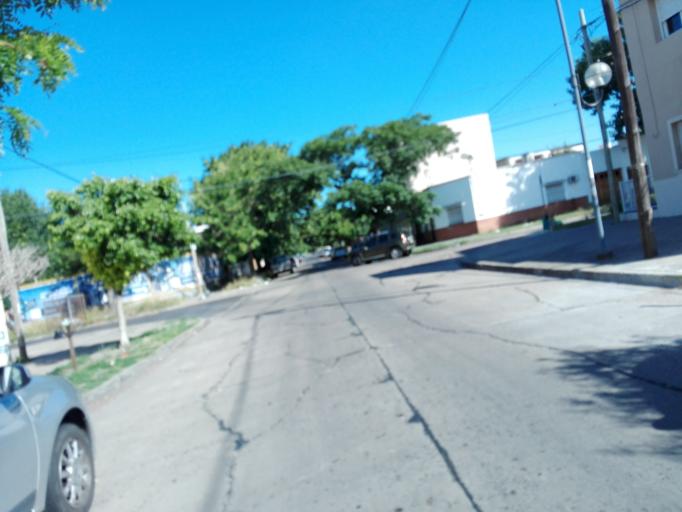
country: AR
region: Buenos Aires
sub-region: Partido de La Plata
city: La Plata
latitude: -34.9471
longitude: -57.9522
